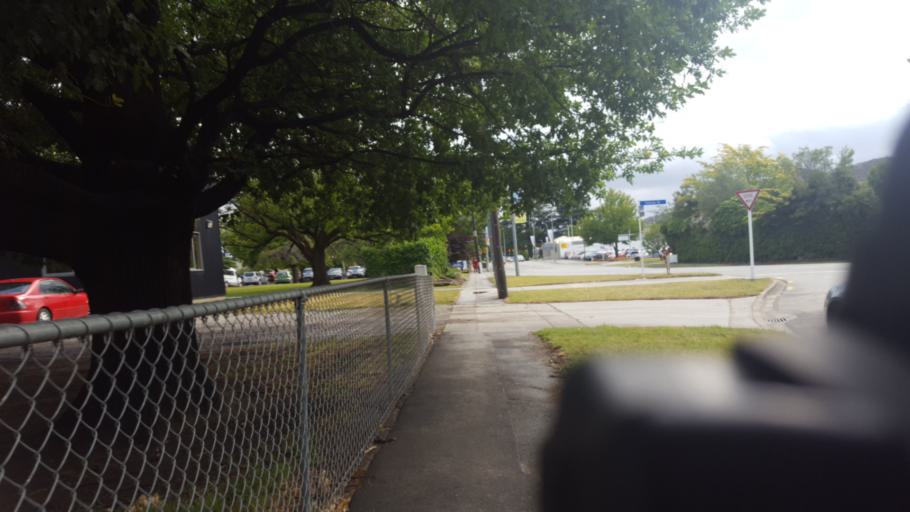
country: NZ
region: Otago
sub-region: Queenstown-Lakes District
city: Wanaka
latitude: -45.2562
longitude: 169.3901
